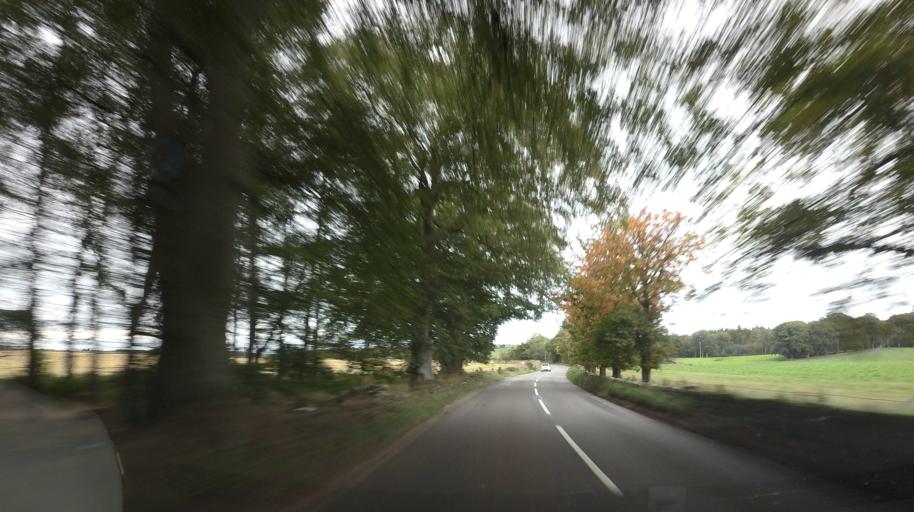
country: GB
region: Scotland
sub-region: Aberdeenshire
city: Kemnay
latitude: 57.1691
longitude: -2.4205
